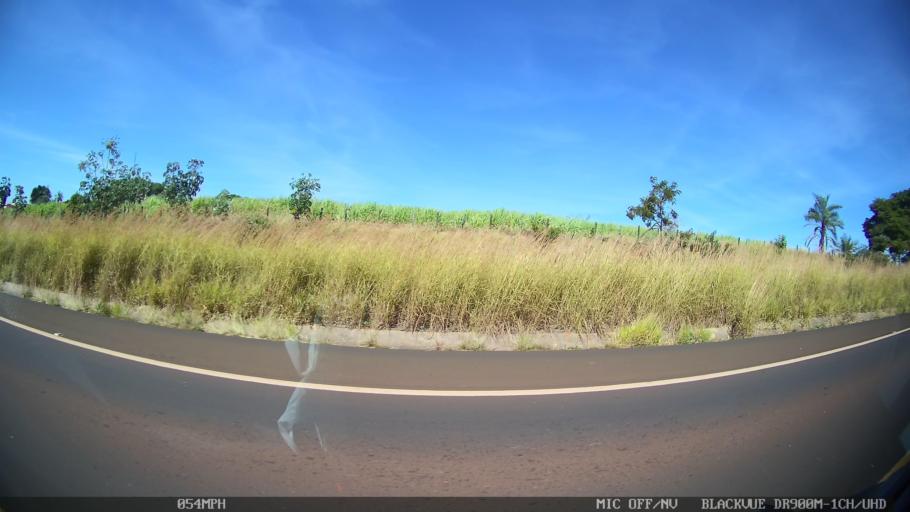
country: BR
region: Sao Paulo
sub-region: Franca
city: Franca
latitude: -20.5604
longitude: -47.5054
